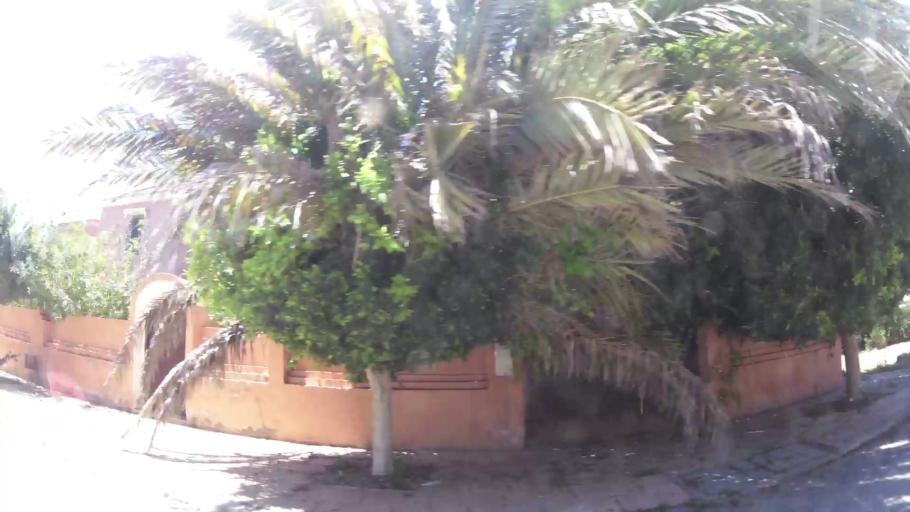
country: MA
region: Oriental
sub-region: Berkane-Taourirt
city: Madagh
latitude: 35.0866
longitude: -2.2346
